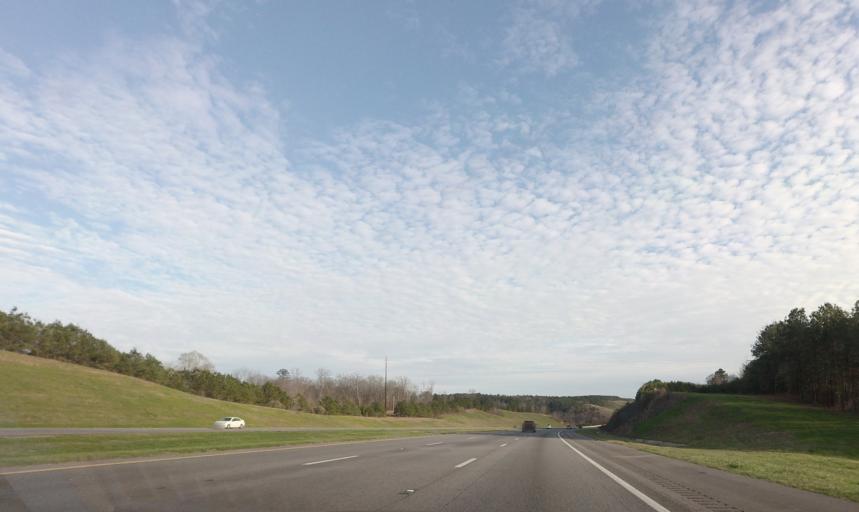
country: US
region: Alabama
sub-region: Walker County
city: Cordova
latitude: 33.7121
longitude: -87.1501
